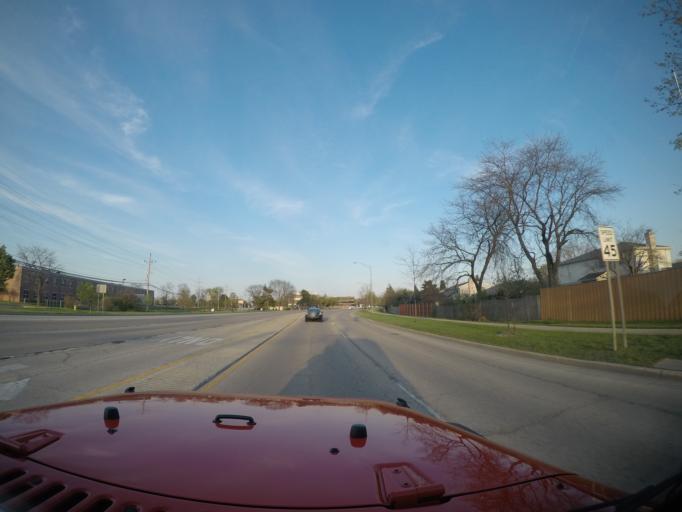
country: US
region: Illinois
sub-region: Cook County
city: Northbrook
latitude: 42.0875
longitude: -87.8530
